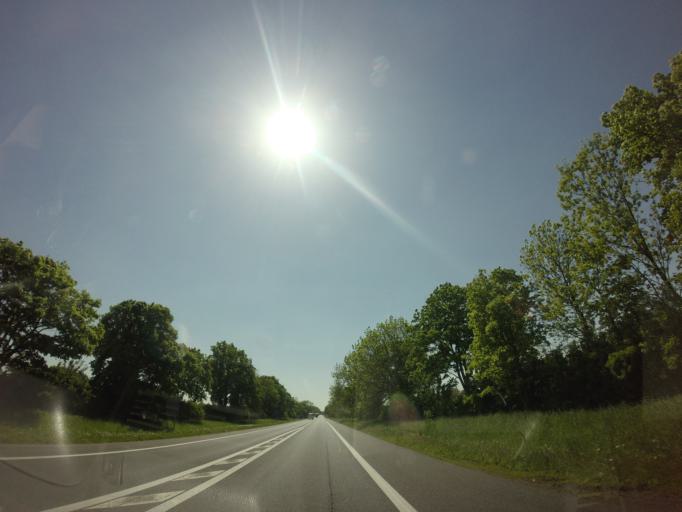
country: PL
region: West Pomeranian Voivodeship
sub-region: Powiat pyrzycki
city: Lipiany
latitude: 52.9858
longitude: 14.9788
